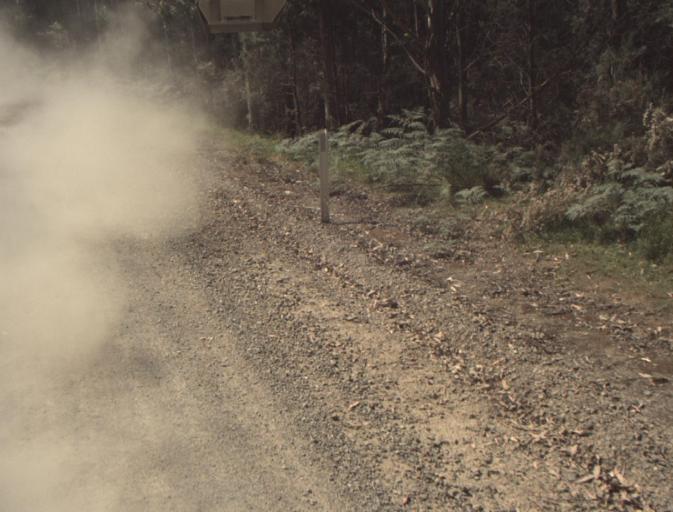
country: AU
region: Tasmania
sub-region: Dorset
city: Scottsdale
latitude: -41.3631
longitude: 147.4654
